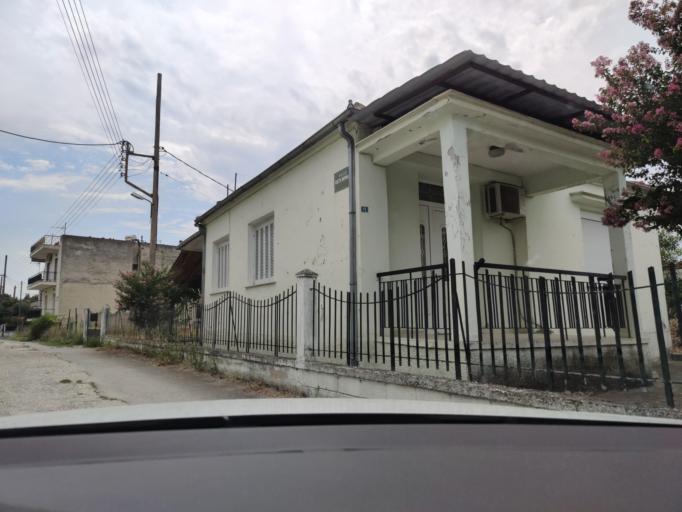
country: GR
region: Central Macedonia
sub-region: Nomos Serron
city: Serres
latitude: 41.0798
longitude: 23.5362
